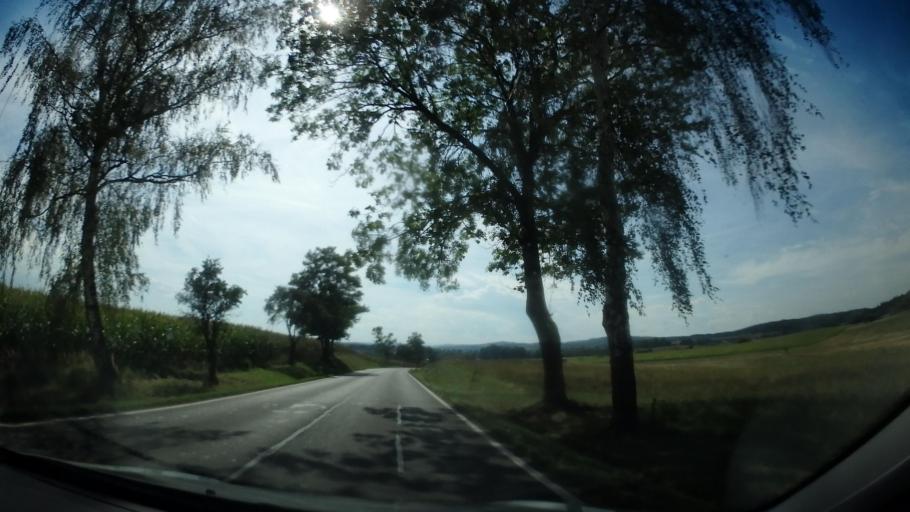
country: CZ
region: Jihocesky
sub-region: Okres Pisek
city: Pisek
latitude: 49.3008
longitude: 14.0635
